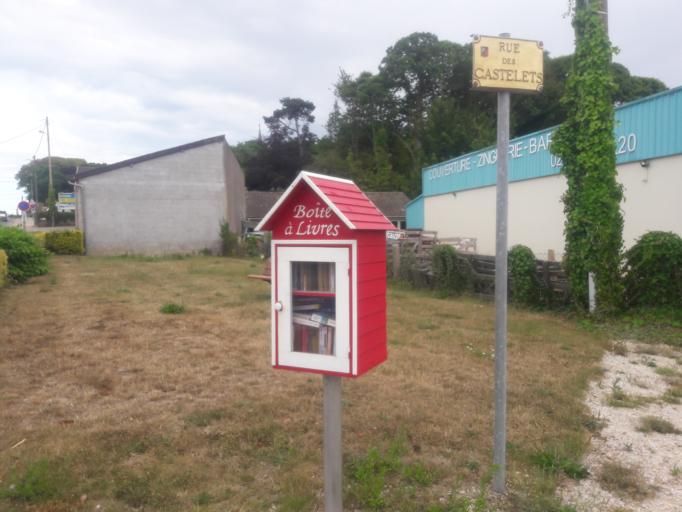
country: FR
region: Lower Normandy
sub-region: Departement de la Manche
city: Saint-Pierre-Eglise
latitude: 49.6667
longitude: -1.3986
